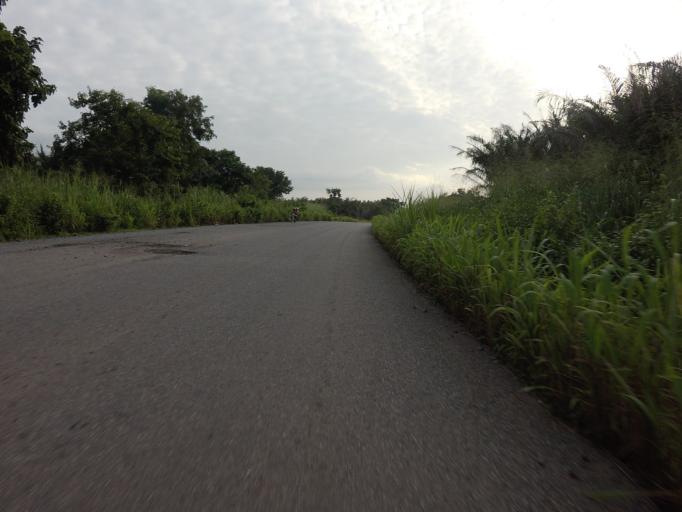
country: GH
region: Volta
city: Kpandu
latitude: 6.8676
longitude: 0.4103
